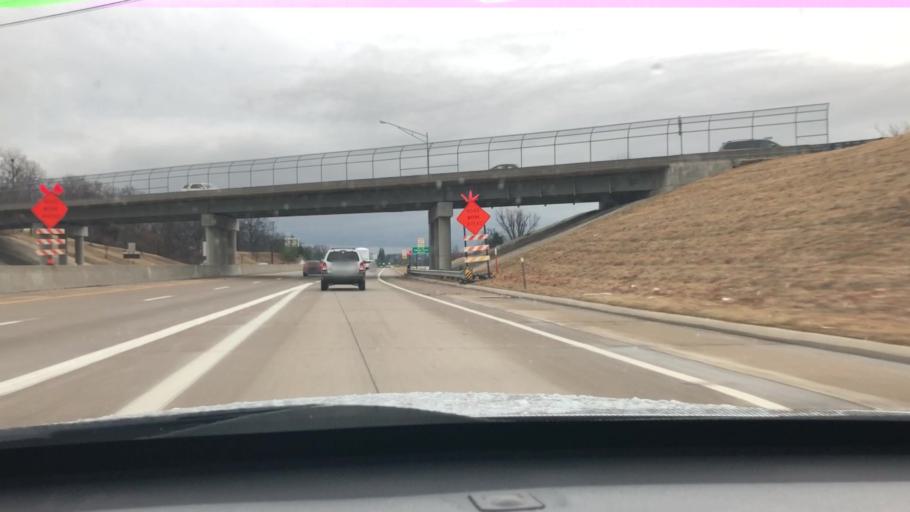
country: US
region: Missouri
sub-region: Saint Louis County
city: Valley Park
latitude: 38.5644
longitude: -90.4980
